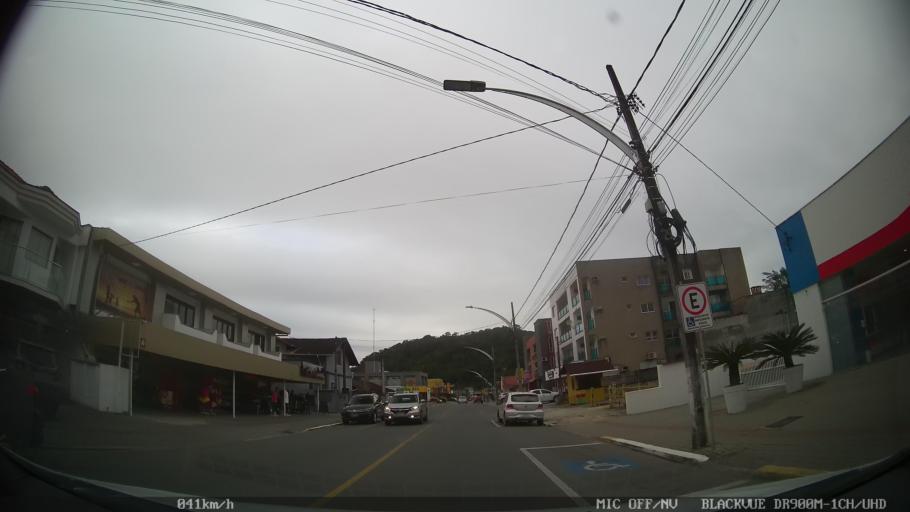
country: BR
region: Santa Catarina
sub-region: Joinville
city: Joinville
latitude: -26.2082
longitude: -48.9087
